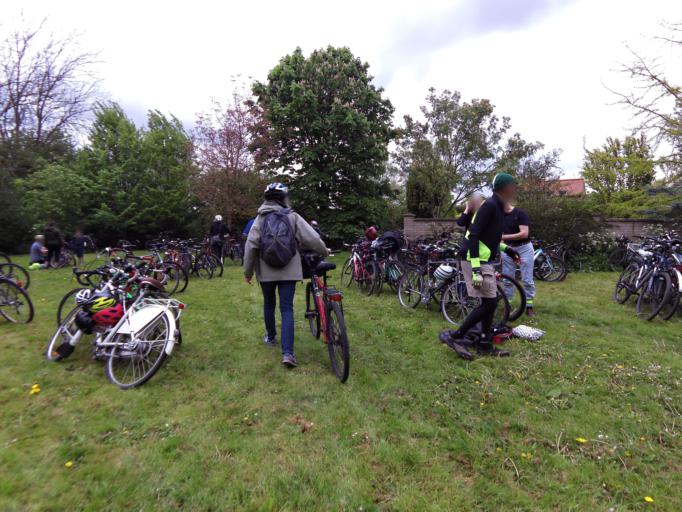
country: GB
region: England
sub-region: Cambridgeshire
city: Bottisham
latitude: 52.2730
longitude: 0.2925
